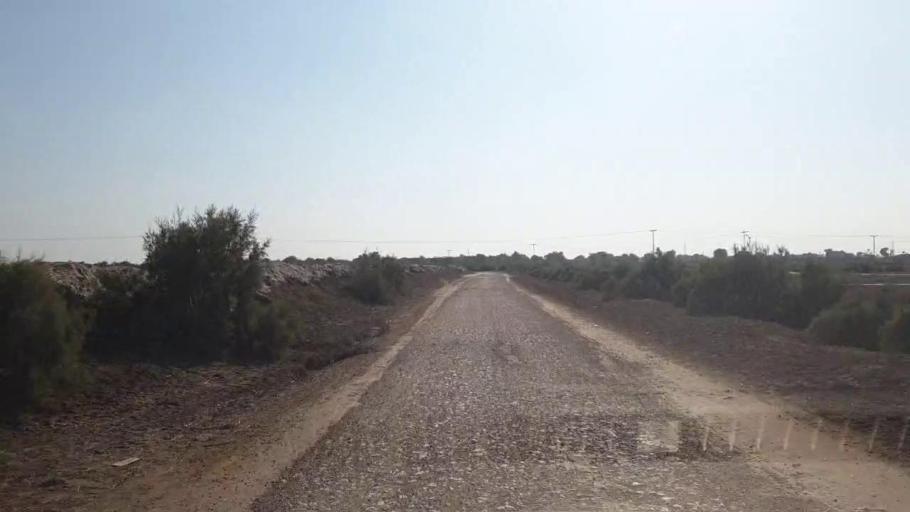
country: PK
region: Sindh
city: Shahpur Chakar
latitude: 26.1529
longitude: 68.6771
